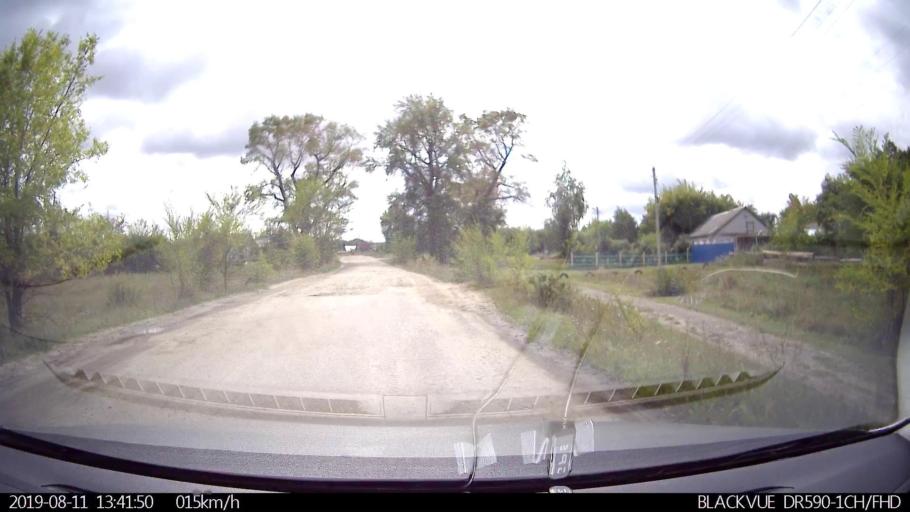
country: RU
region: Ulyanovsk
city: Ignatovka
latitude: 53.8570
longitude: 47.5756
